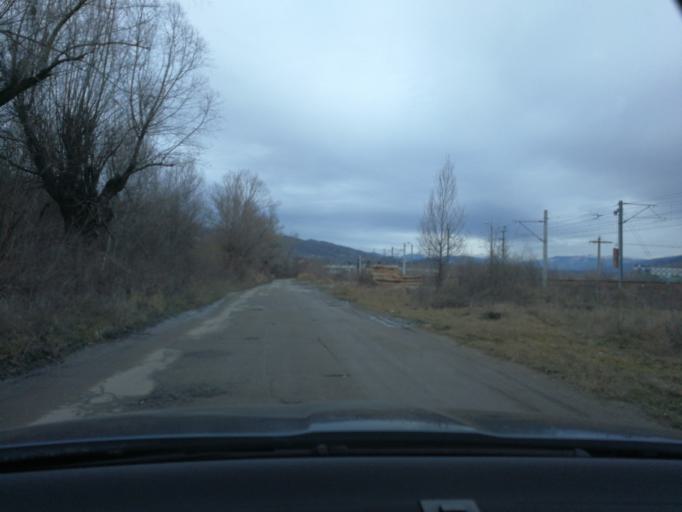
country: RO
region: Prahova
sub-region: Comuna Poiana Campina
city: Poiana Campina
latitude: 45.1387
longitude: 25.7004
